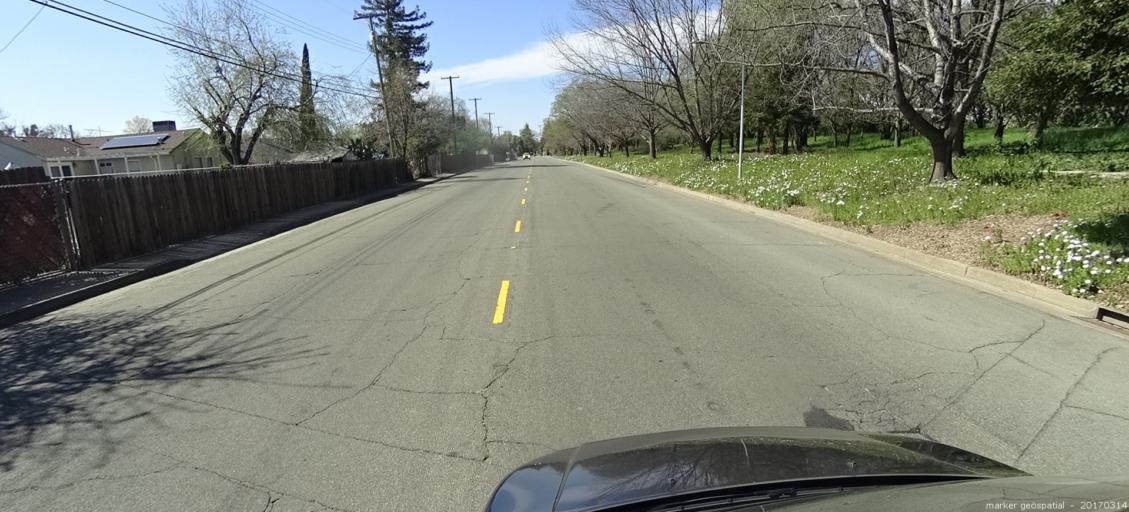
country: US
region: California
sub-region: Sacramento County
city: Parkway
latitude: 38.5211
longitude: -121.5022
